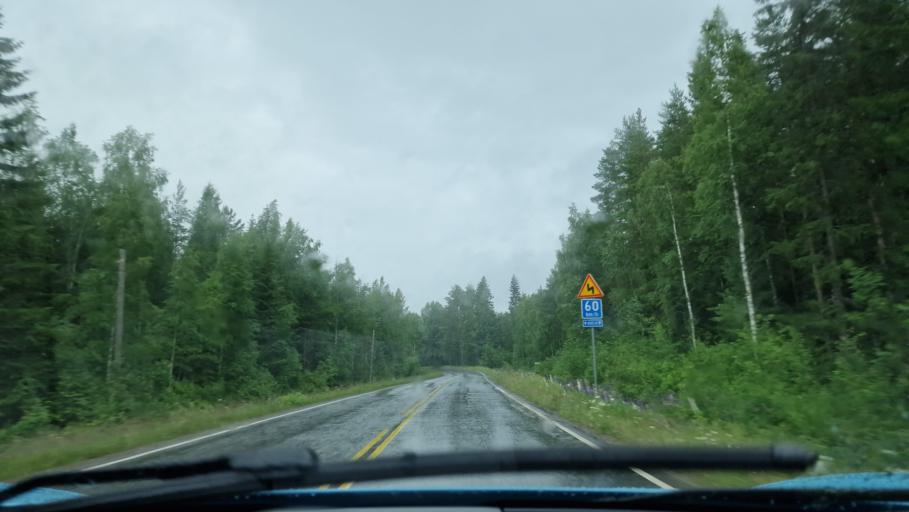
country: FI
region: Southern Ostrobothnia
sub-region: Jaerviseutu
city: Soini
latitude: 62.8267
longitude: 24.3418
